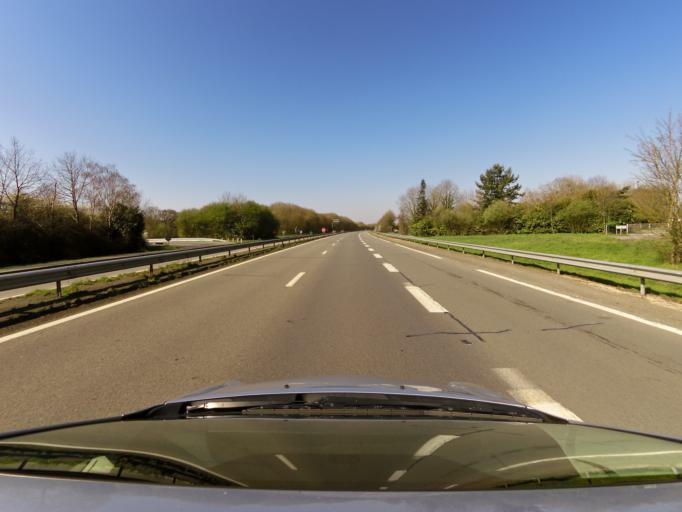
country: FR
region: Brittany
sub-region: Departement d'Ille-et-Vilaine
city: Mordelles
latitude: 48.0676
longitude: -1.8233
